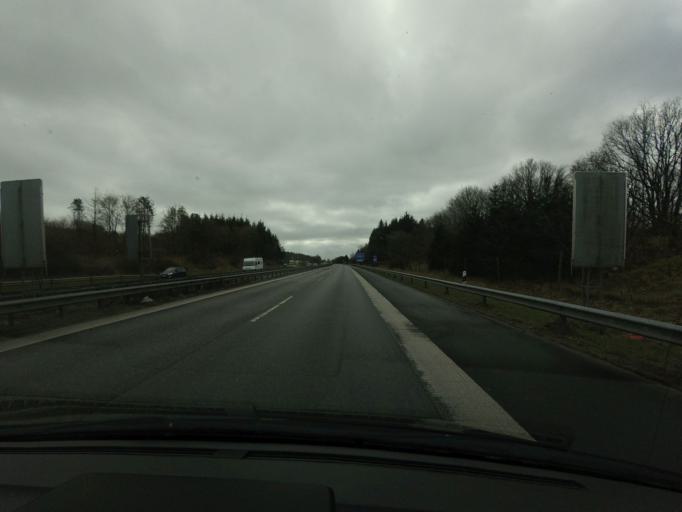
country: DE
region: Schleswig-Holstein
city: Neu Duvenstedt
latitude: 54.3681
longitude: 9.6673
